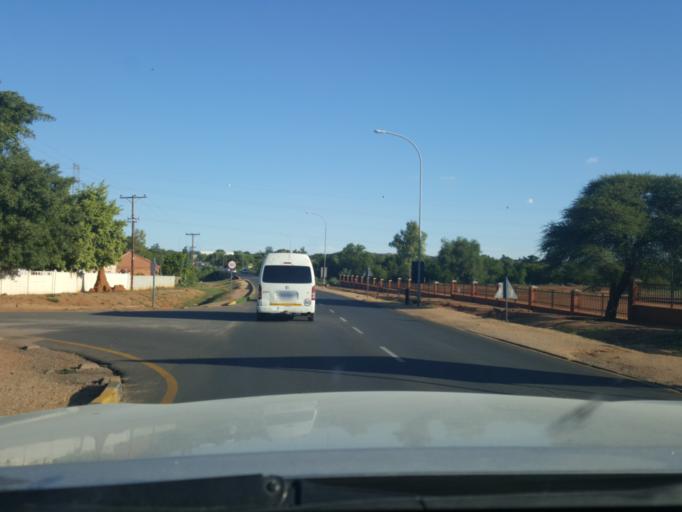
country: BW
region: South East
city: Gaborone
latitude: -24.6354
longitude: 25.9389
